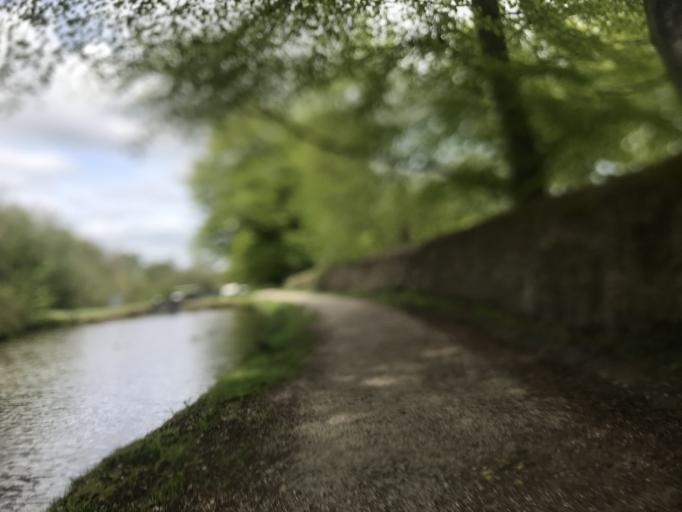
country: GB
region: England
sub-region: Borough of Stockport
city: Marple
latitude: 53.3995
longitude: -2.0583
